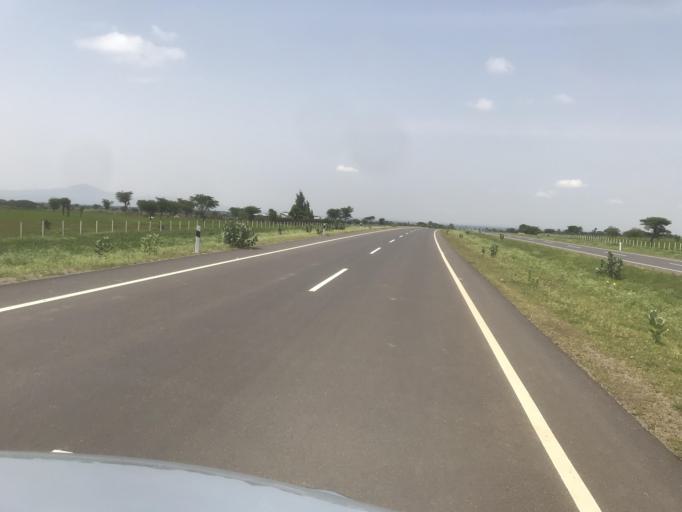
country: ET
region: Oromiya
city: Mojo
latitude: 8.4742
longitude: 39.0467
